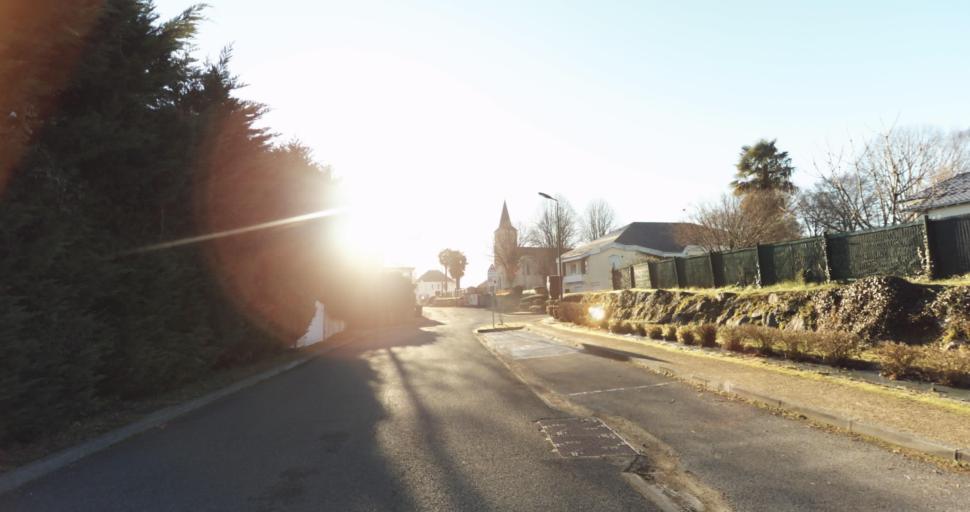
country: FR
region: Aquitaine
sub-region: Departement des Pyrenees-Atlantiques
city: Morlaas
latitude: 43.3278
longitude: -0.2593
